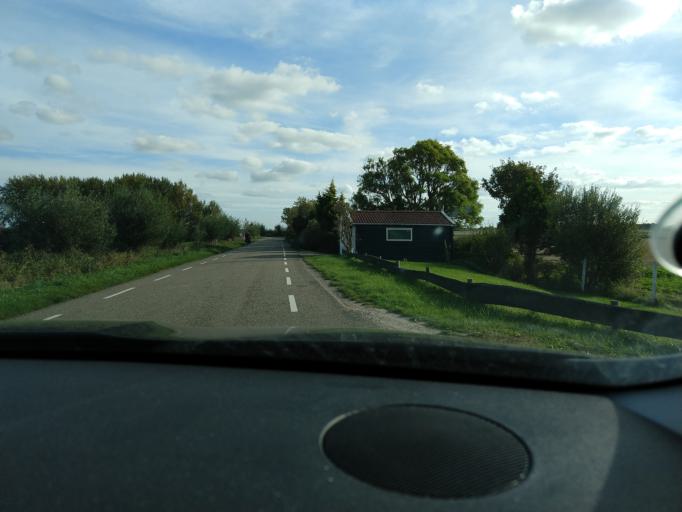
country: NL
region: Zeeland
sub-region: Gemeente Noord-Beveland
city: Kamperland
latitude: 51.5826
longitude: 3.6740
